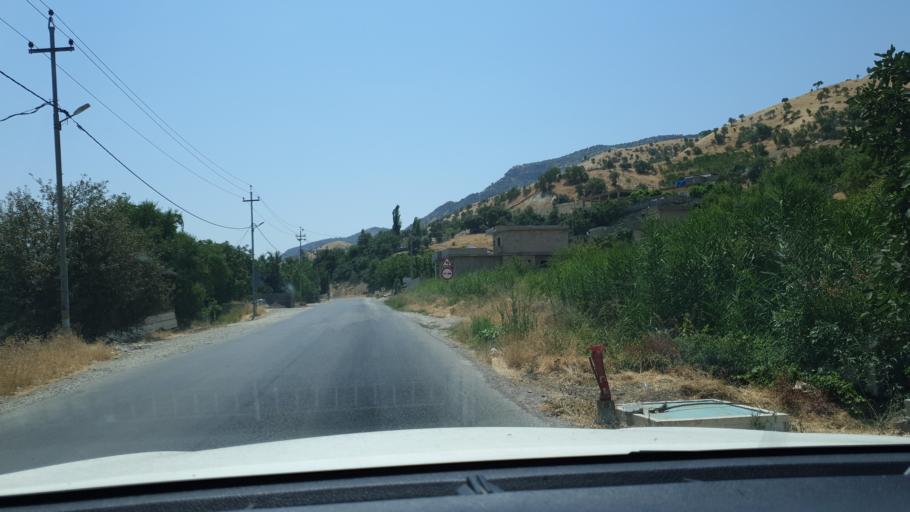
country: IQ
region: Arbil
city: Nahiyat Hiran
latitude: 36.2947
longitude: 44.4751
